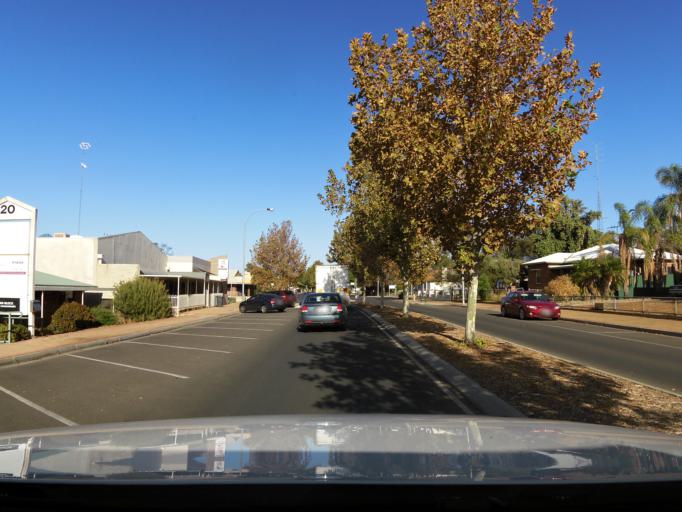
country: AU
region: South Australia
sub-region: Berri and Barmera
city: Berri
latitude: -34.2833
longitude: 140.6047
